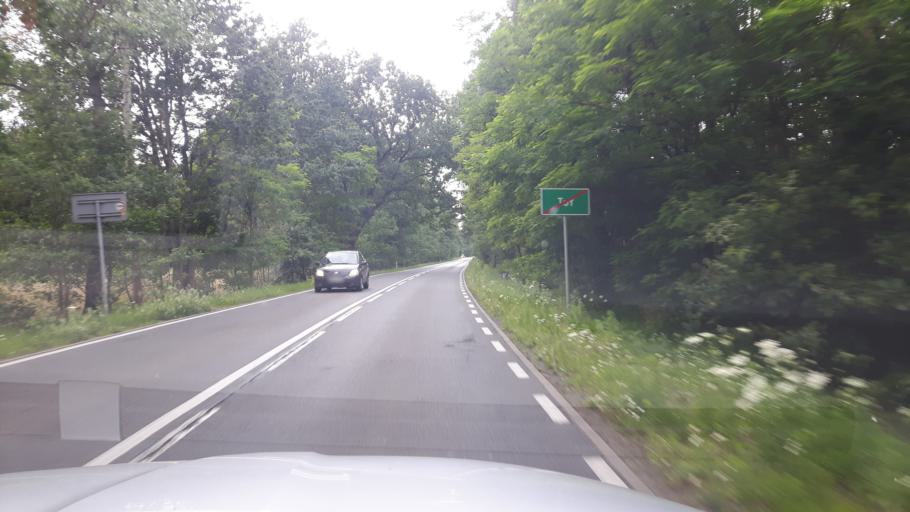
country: PL
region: Masovian Voivodeship
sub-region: Powiat wolominski
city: Ostrowek
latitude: 52.3801
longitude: 21.3865
